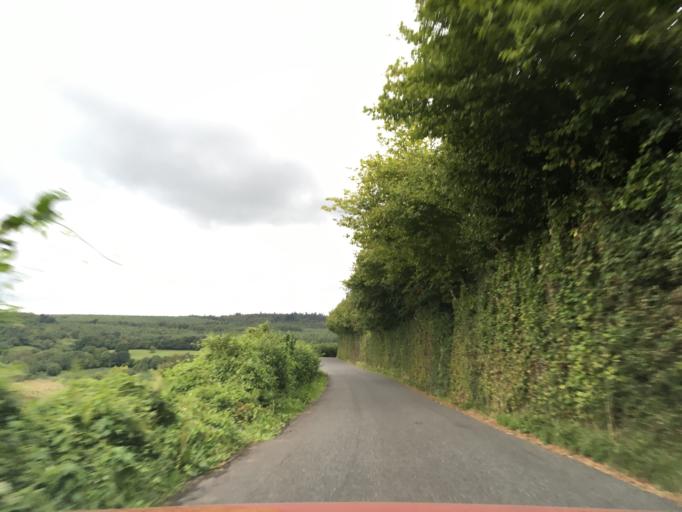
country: GB
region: Wales
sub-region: Newport
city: Llanvaches
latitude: 51.6354
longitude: -2.8220
